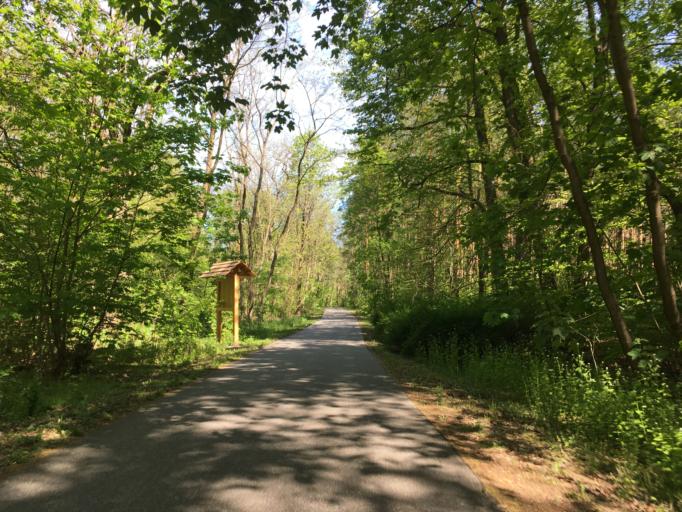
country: DE
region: Brandenburg
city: Bernau bei Berlin
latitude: 52.6941
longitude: 13.5411
